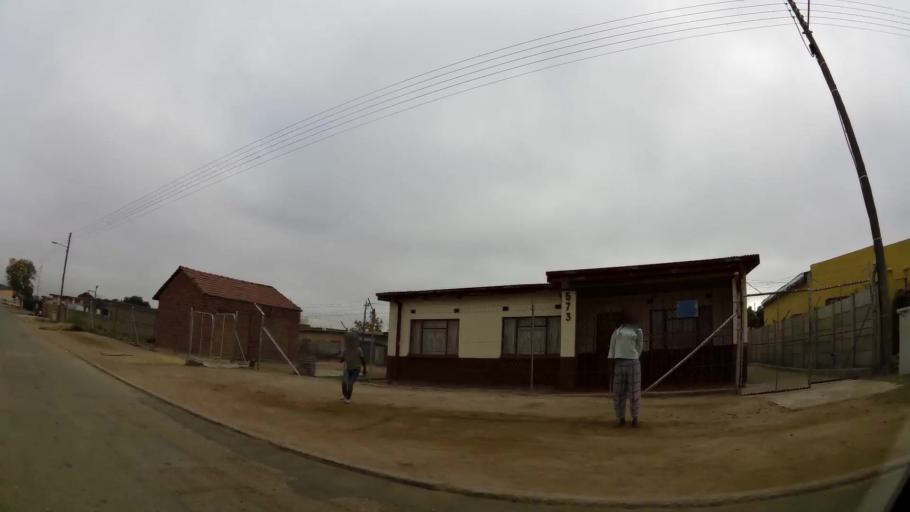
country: ZA
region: Limpopo
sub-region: Capricorn District Municipality
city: Polokwane
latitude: -23.8393
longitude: 29.3868
